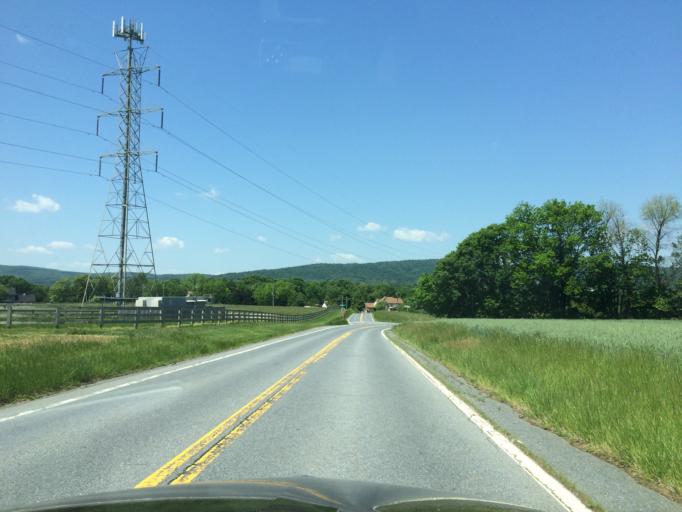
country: US
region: Maryland
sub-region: Frederick County
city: Myersville
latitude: 39.4816
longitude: -77.5594
